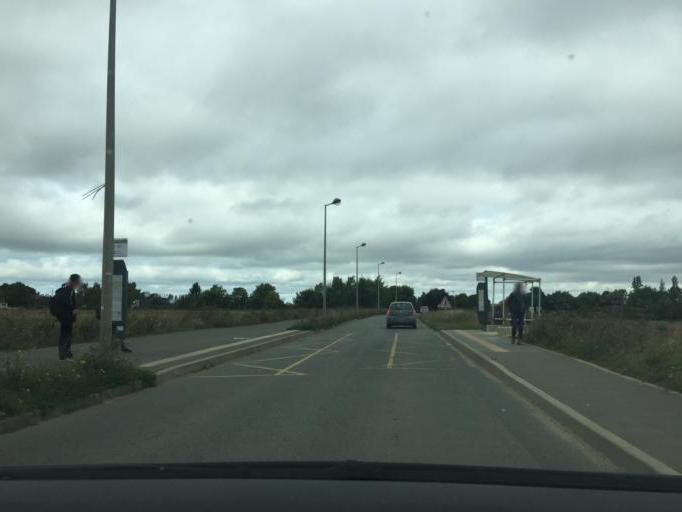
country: FR
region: Ile-de-France
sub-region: Departement de l'Essonne
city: Bures-sur-Yvette
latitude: 48.7123
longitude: 2.1724
